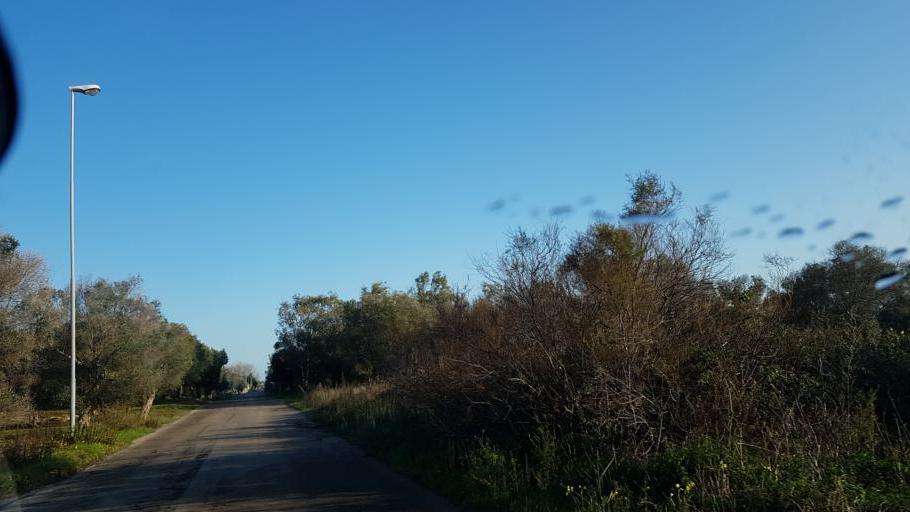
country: IT
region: Apulia
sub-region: Provincia di Brindisi
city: Torchiarolo
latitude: 40.5039
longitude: 18.1062
